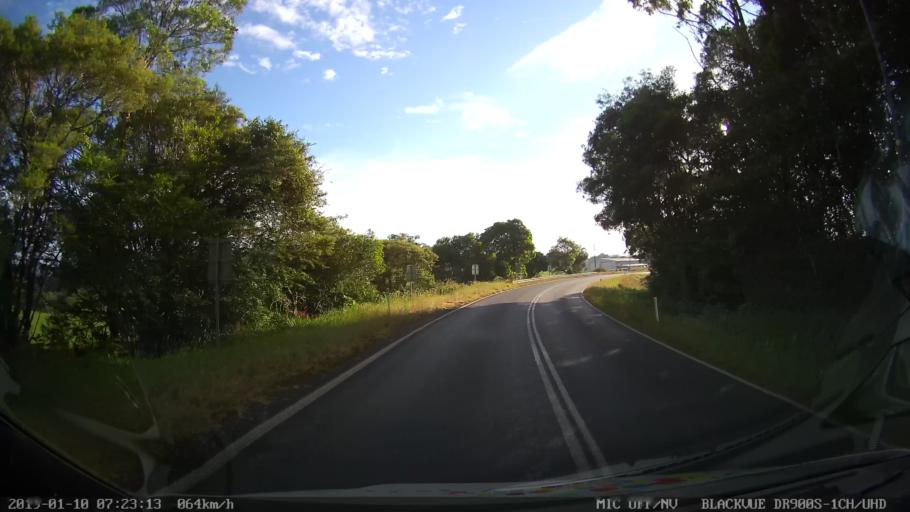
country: AU
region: New South Wales
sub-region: Bellingen
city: Dorrigo
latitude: -30.3794
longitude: 152.5699
